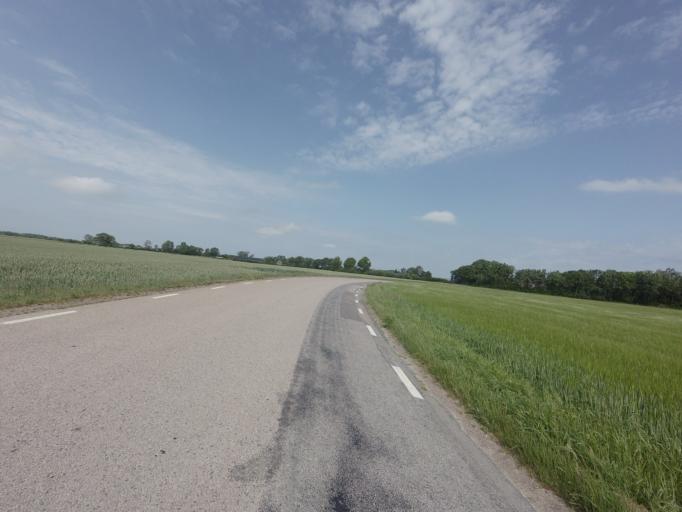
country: SE
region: Skane
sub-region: Hoganas Kommun
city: Hoganas
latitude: 56.1840
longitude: 12.6596
